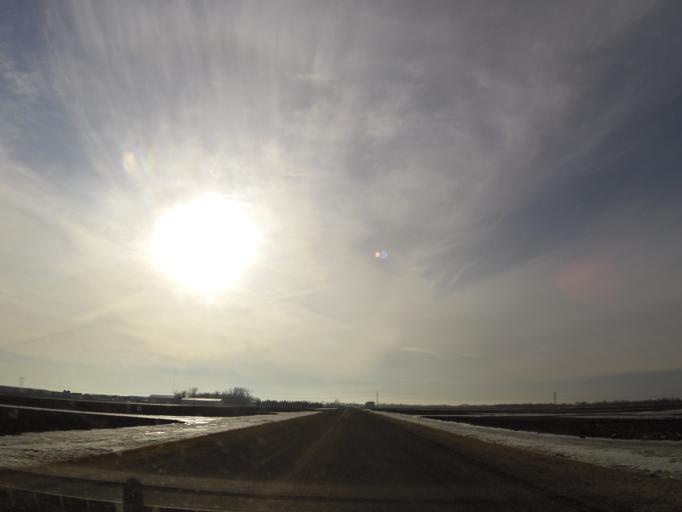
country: US
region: North Dakota
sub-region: Walsh County
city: Grafton
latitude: 48.4265
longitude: -97.2588
